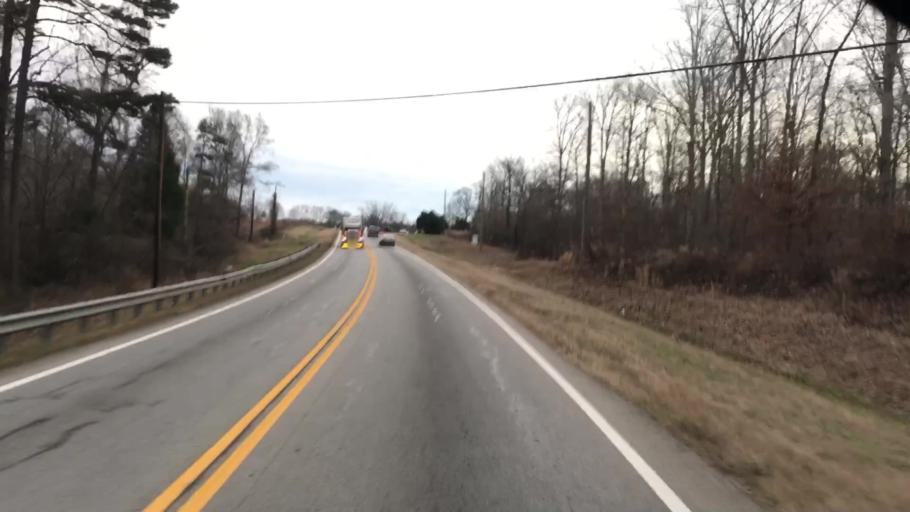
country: US
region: Georgia
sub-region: Jackson County
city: Hoschton
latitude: 34.0504
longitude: -83.7788
